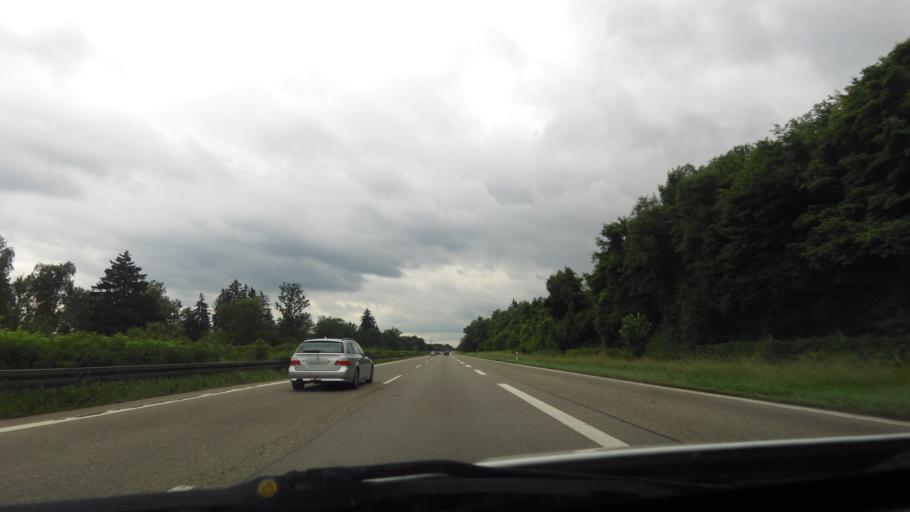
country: DE
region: Baden-Wuerttemberg
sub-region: Tuebingen Region
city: Kirchdorf
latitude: 48.0825
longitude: 10.1371
